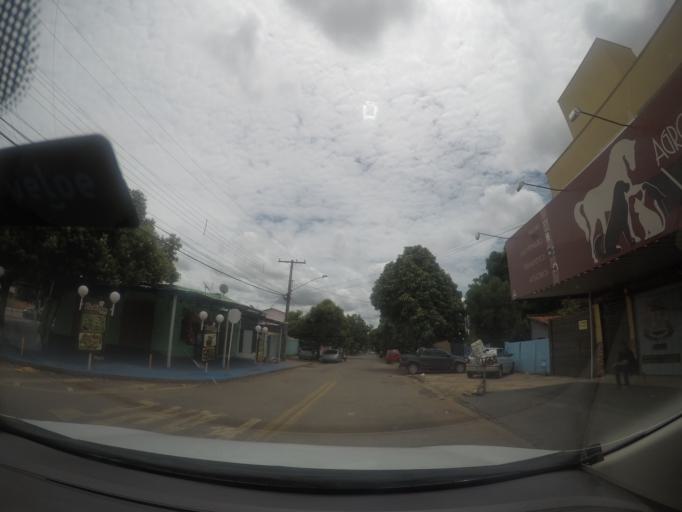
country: BR
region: Goias
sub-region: Goiania
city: Goiania
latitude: -16.7026
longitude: -49.3310
